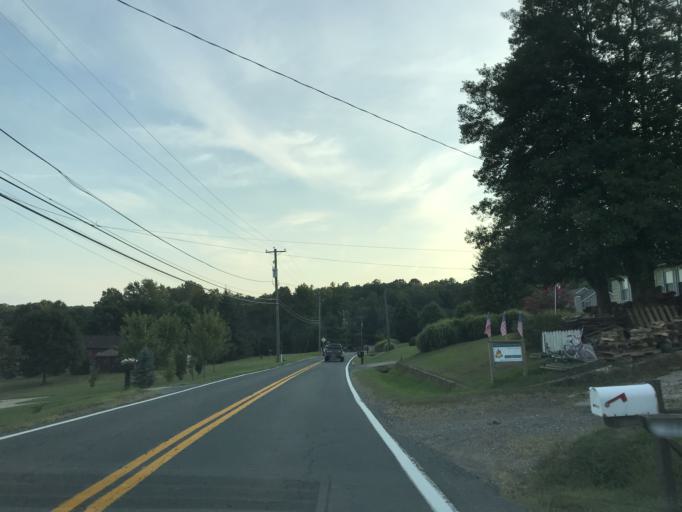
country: US
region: Maryland
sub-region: Cecil County
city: Charlestown
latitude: 39.5113
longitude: -75.9525
